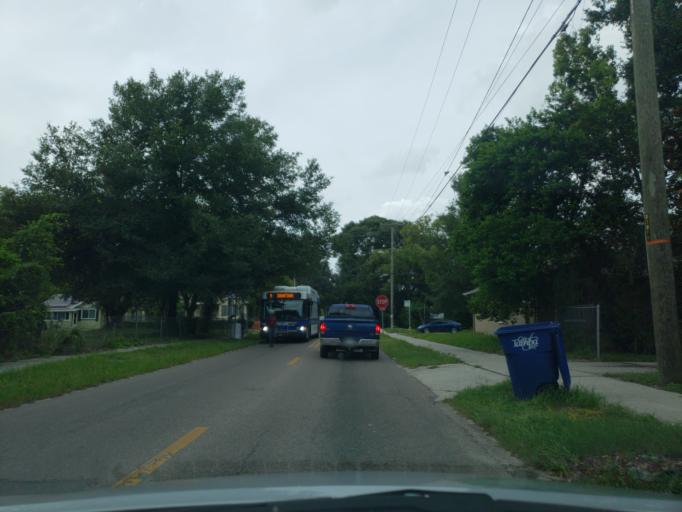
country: US
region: Florida
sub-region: Hillsborough County
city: Tampa
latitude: 27.9846
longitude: -82.4430
